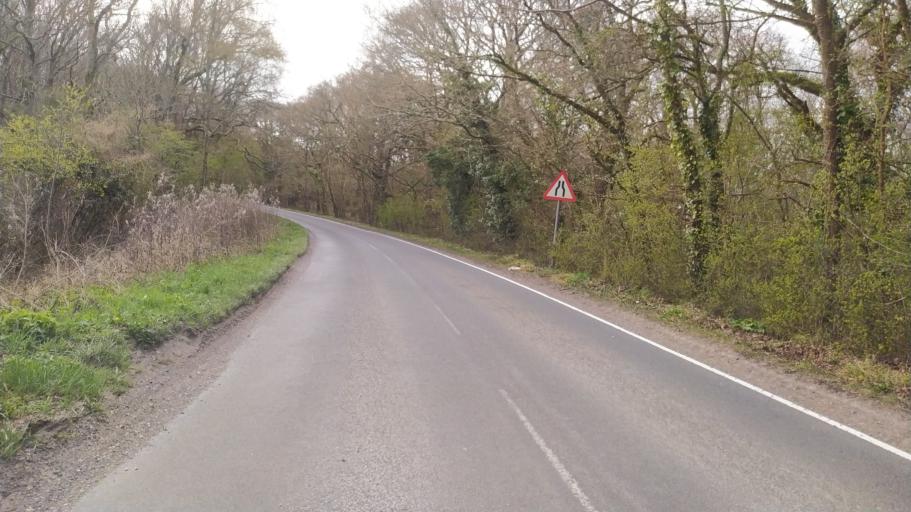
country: GB
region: England
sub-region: Hampshire
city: Wickham
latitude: 50.8882
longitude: -1.2176
